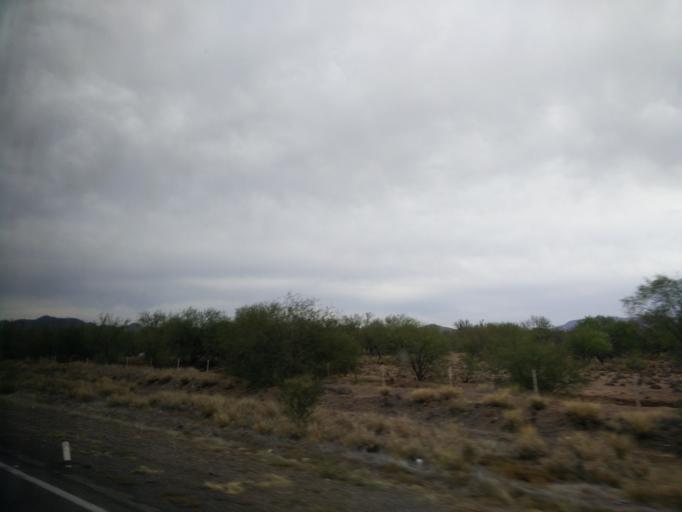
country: MX
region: Sonora
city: Hermosillo
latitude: 28.9064
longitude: -110.9511
